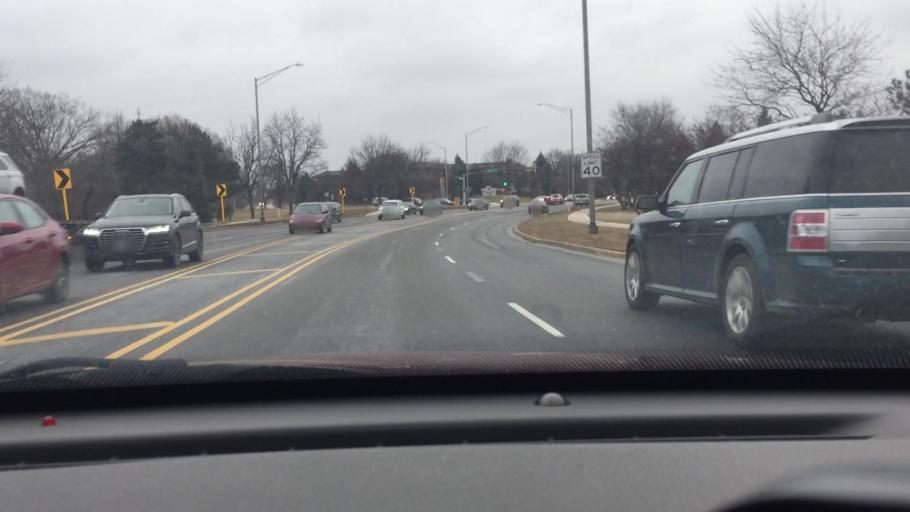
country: US
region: Illinois
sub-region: DuPage County
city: Warrenville
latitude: 41.7861
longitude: -88.1835
